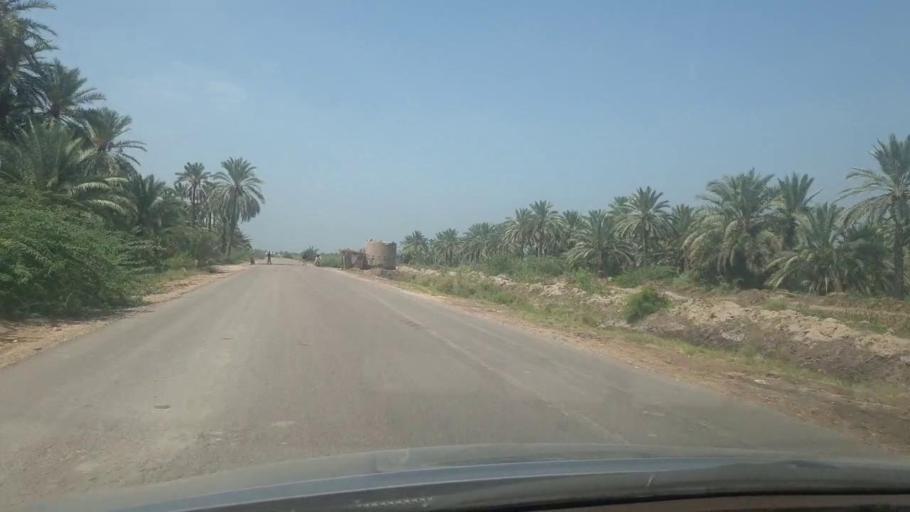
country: PK
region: Sindh
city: Ranipur
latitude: 27.2422
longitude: 68.5750
